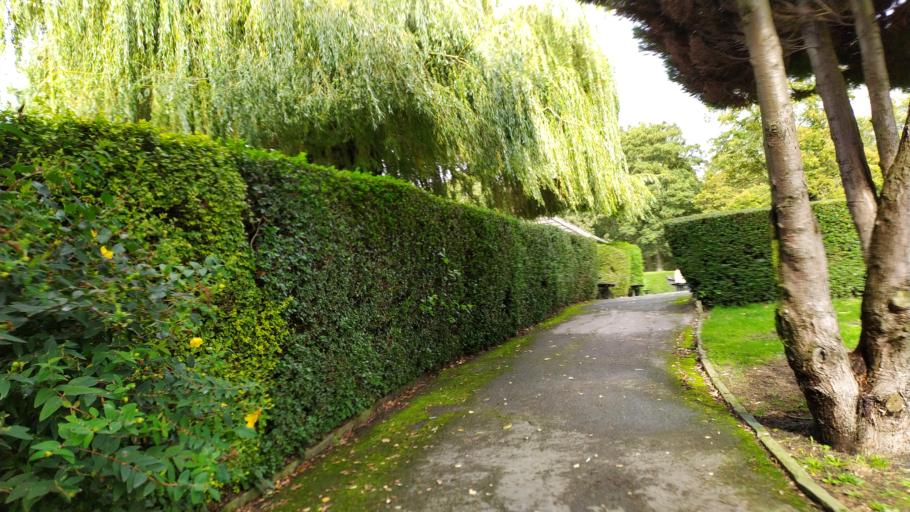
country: GB
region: England
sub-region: City and Borough of Leeds
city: Leeds
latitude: 53.8094
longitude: -1.5618
